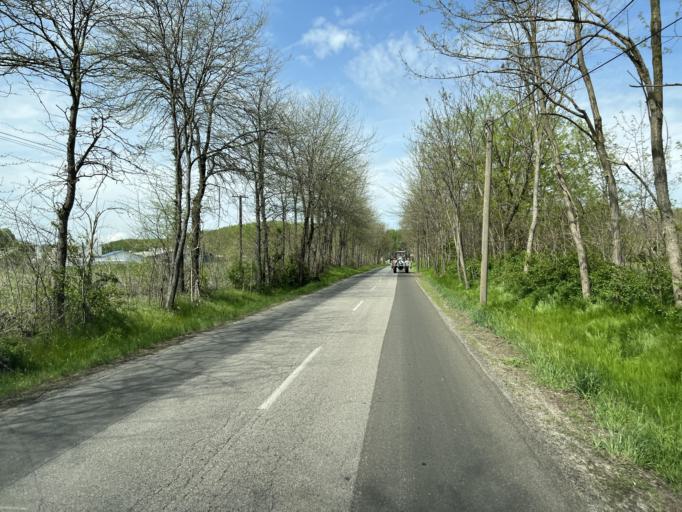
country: HU
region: Pest
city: Albertirsa
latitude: 47.2180
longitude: 19.6094
